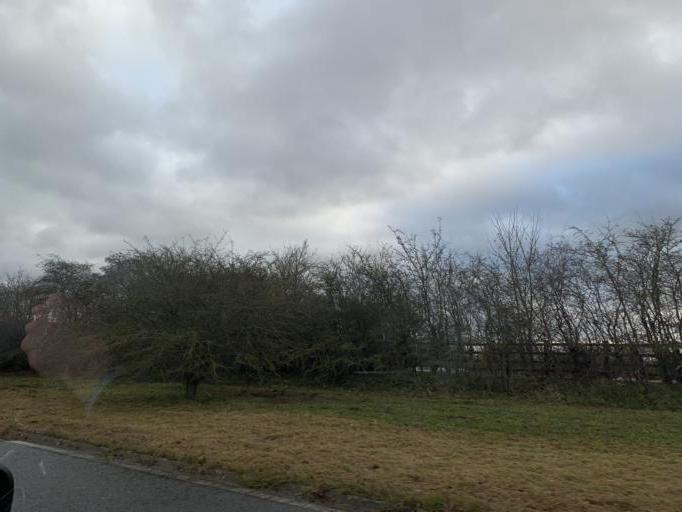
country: GB
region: England
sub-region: City of York
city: Copmanthorpe
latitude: 53.9227
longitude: -1.1317
